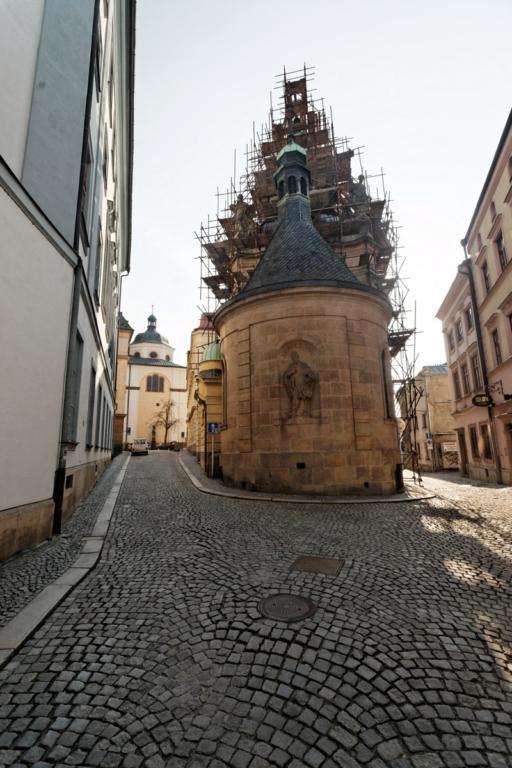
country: CZ
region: Olomoucky
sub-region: Okres Olomouc
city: Olomouc
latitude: 49.5947
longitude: 17.2547
